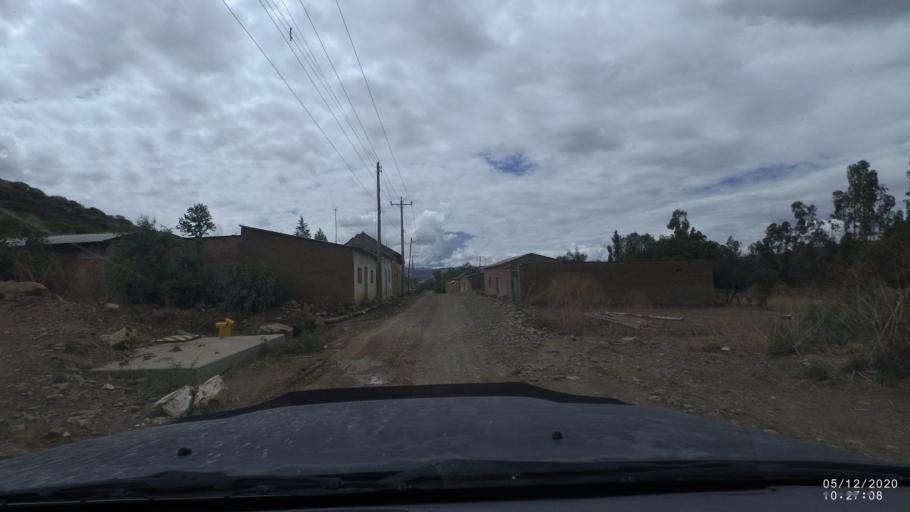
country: BO
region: Cochabamba
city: Sipe Sipe
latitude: -17.5310
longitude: -66.2798
